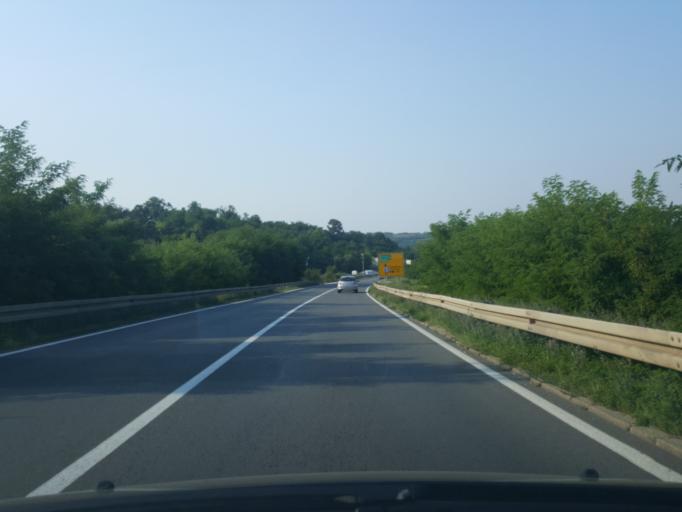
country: RS
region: Central Serbia
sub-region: Belgrade
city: Sopot
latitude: 44.5580
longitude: 20.6674
